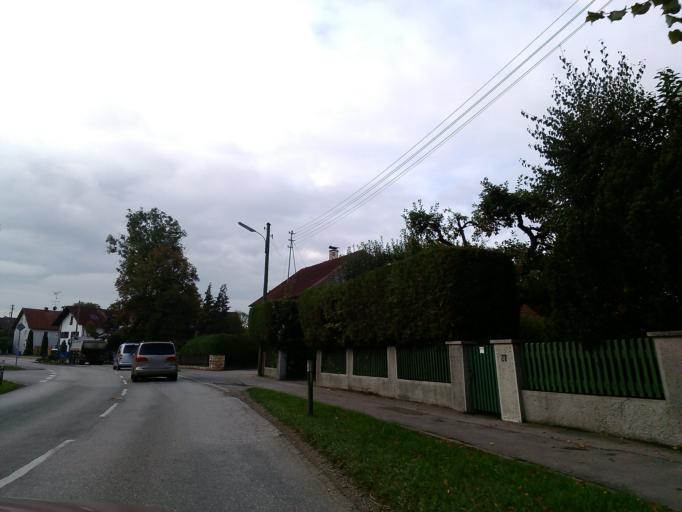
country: DE
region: Bavaria
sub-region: Upper Bavaria
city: Alling
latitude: 48.1446
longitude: 11.3012
